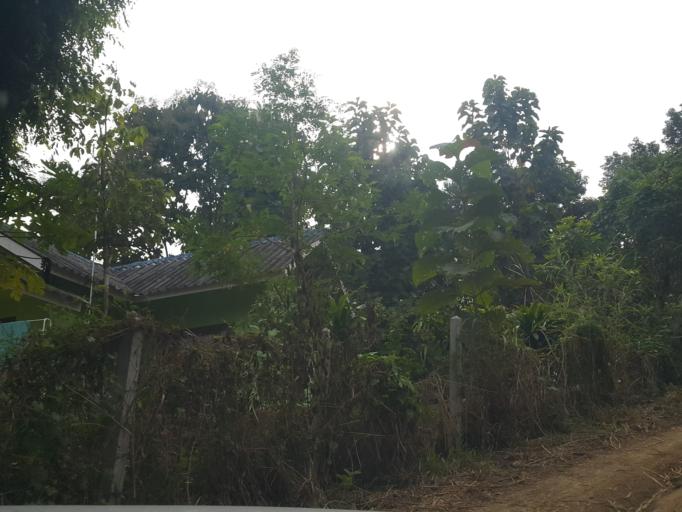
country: TH
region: Chiang Mai
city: Pai
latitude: 19.3654
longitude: 98.4471
